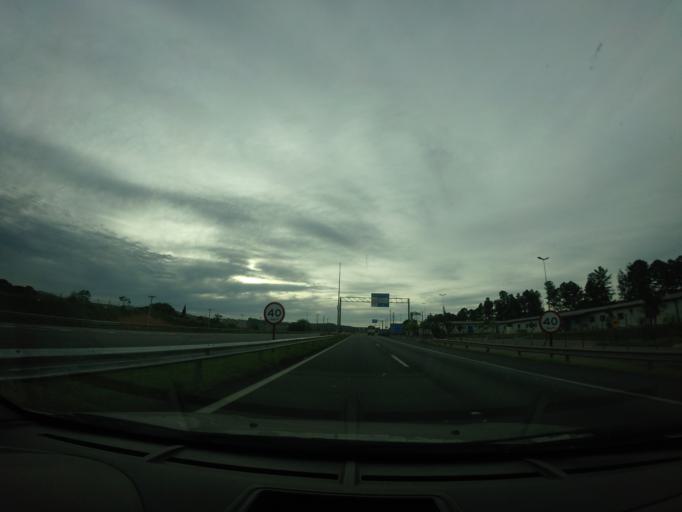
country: BR
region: Sao Paulo
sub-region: Itatiba
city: Itatiba
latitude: -22.9520
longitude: -46.8630
